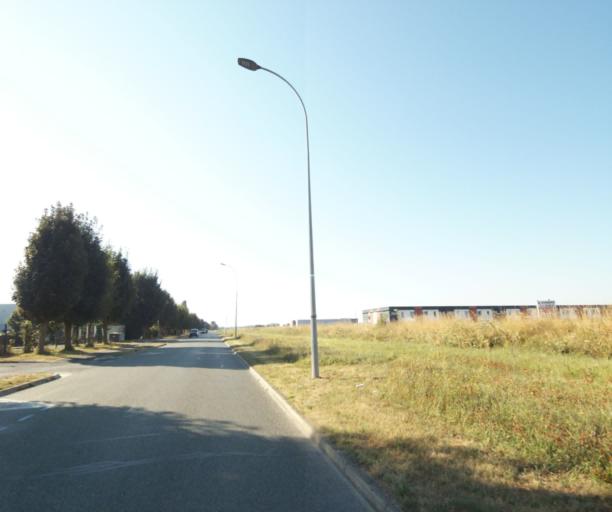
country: FR
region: Ile-de-France
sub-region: Departement de Seine-et-Marne
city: Lieusaint
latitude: 48.6215
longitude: 2.5645
